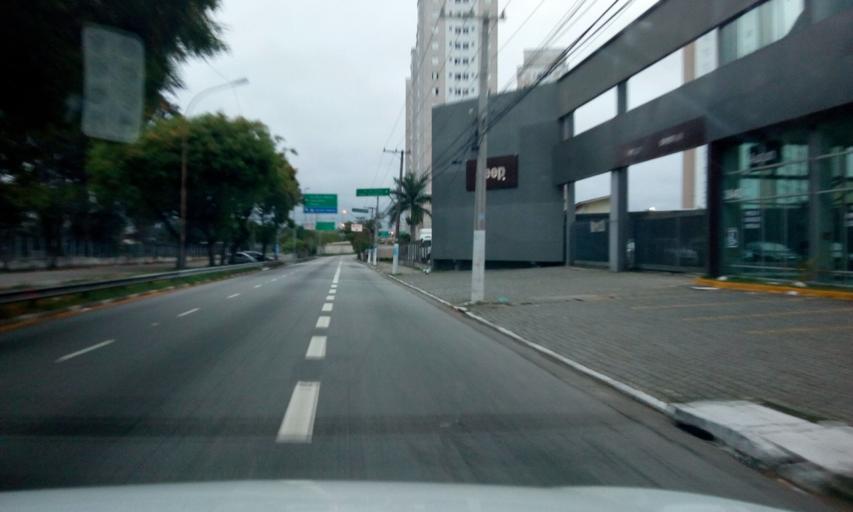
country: BR
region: Sao Paulo
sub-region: Guarulhos
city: Guarulhos
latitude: -23.5260
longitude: -46.5632
